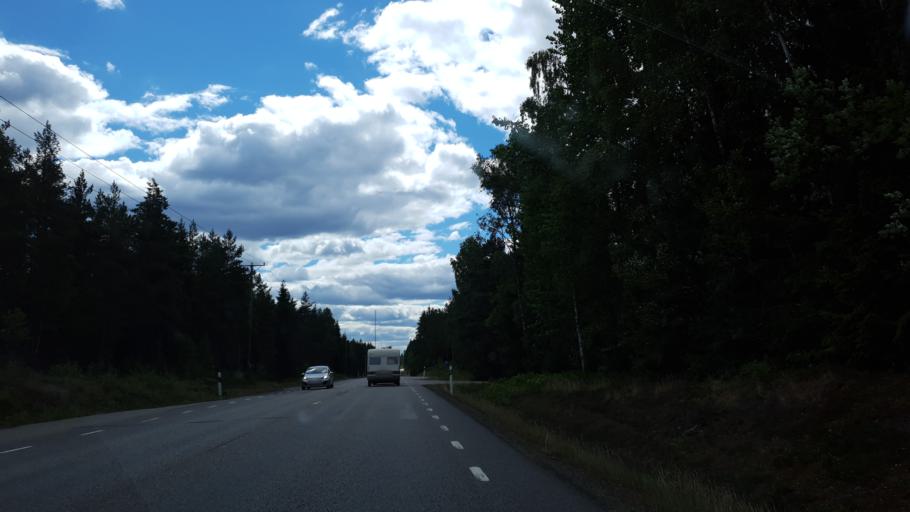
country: SE
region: Kronoberg
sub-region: Vaxjo Kommun
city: Braas
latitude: 57.1422
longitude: 15.1663
